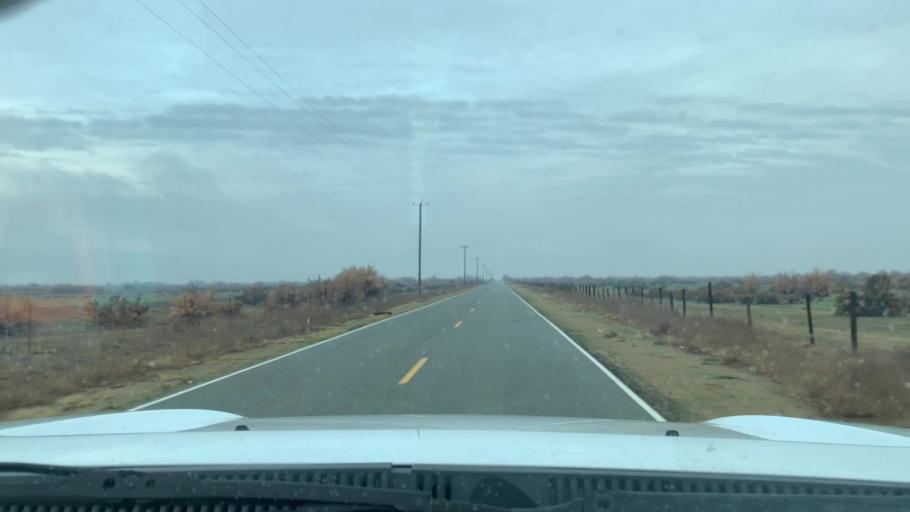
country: US
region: California
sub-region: Kern County
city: Lost Hills
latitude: 35.7066
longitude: -119.5796
